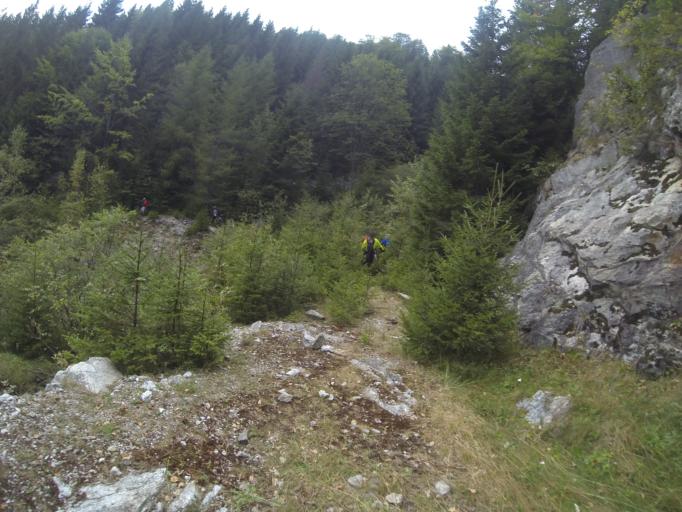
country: RO
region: Gorj
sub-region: Comuna Polovragi
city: Polovragi
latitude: 45.2755
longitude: 23.8292
